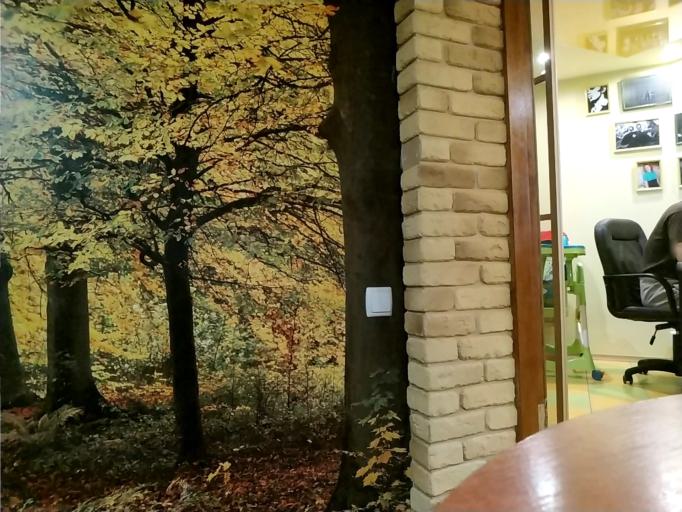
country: RU
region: Tverskaya
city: Zapadnaya Dvina
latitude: 56.3342
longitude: 31.8759
